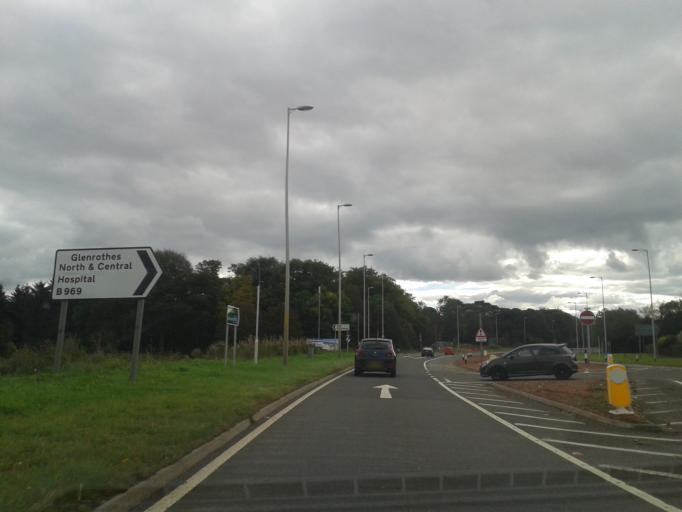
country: GB
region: Scotland
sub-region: Fife
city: Markinch
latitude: 56.2182
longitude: -3.1535
